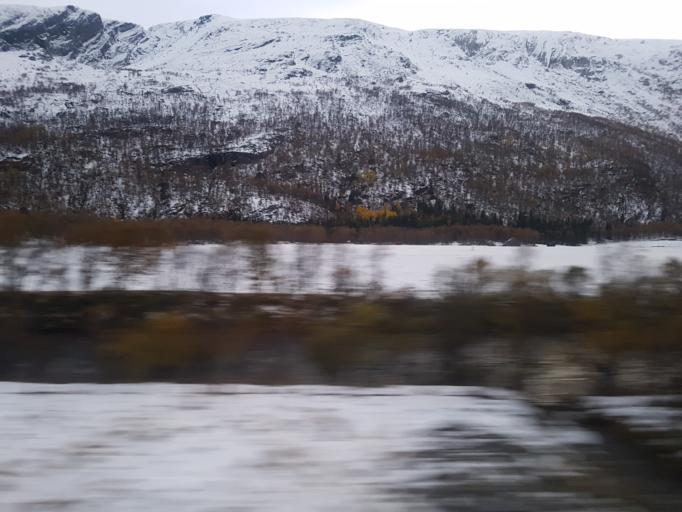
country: NO
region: Sor-Trondelag
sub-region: Oppdal
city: Oppdal
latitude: 62.4166
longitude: 9.6210
